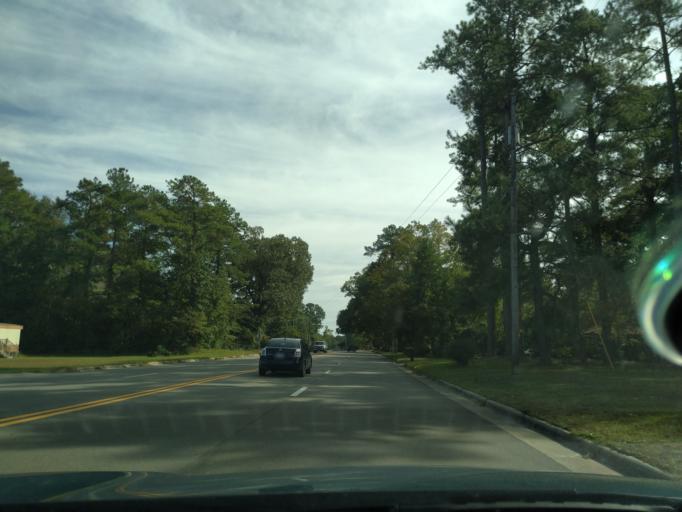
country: US
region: North Carolina
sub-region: Beaufort County
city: River Road
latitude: 35.5252
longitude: -77.0107
